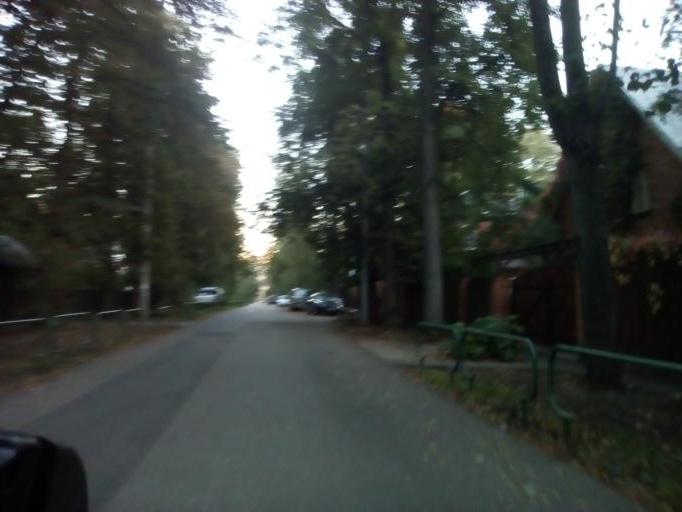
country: RU
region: Moscow
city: Sokol
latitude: 55.8027
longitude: 37.4999
